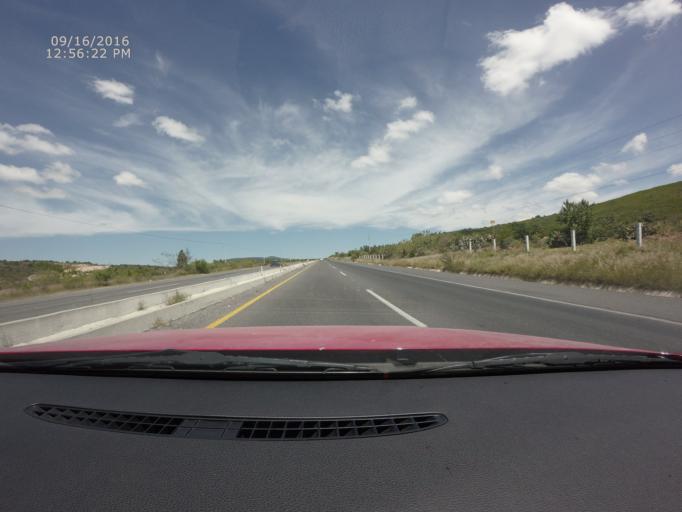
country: MX
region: Queretaro
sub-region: Colon
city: Purisima de Cubos (La Purisima)
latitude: 20.6529
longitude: -100.0992
